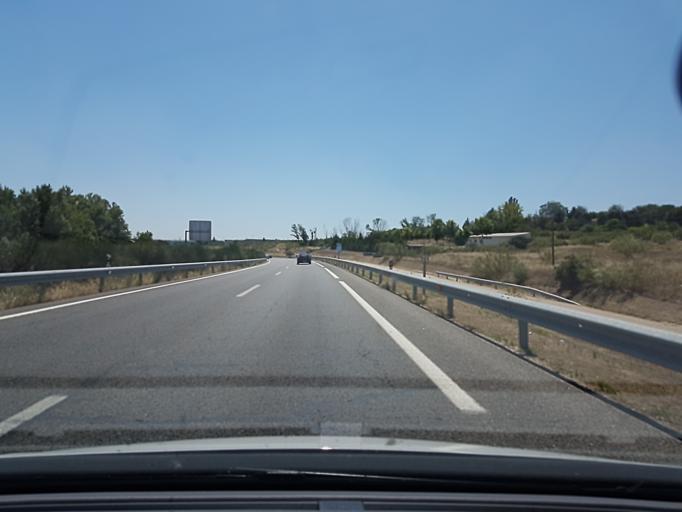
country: ES
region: Madrid
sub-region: Provincia de Madrid
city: Boadilla del Monte
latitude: 40.3875
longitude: -3.9015
